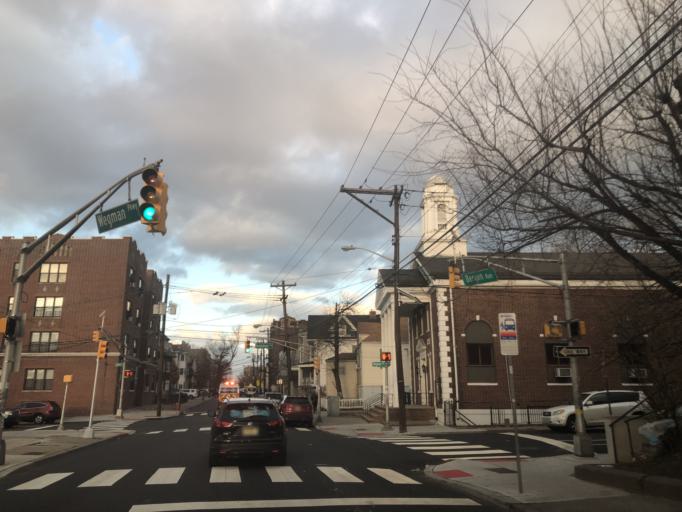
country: US
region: New Jersey
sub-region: Hudson County
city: Jersey City
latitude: 40.7070
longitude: -74.0864
